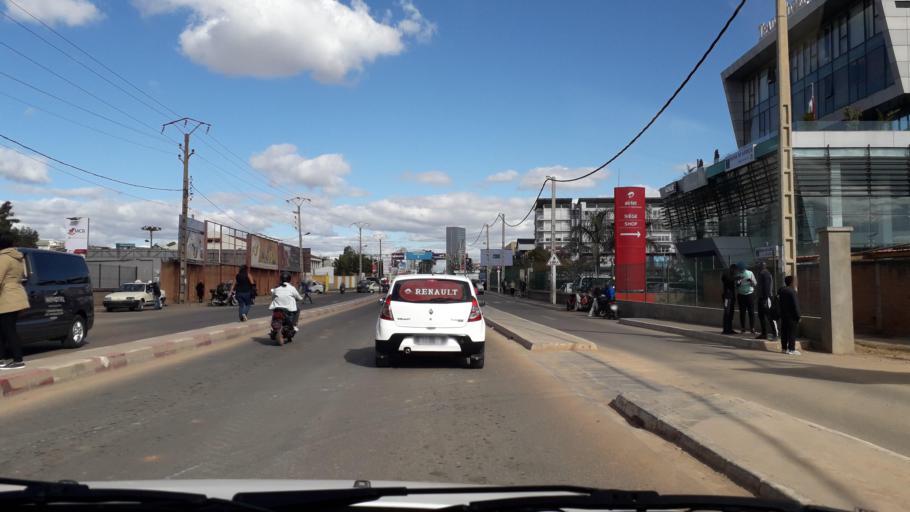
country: MG
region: Analamanga
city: Antananarivo
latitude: -18.8730
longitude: 47.5192
